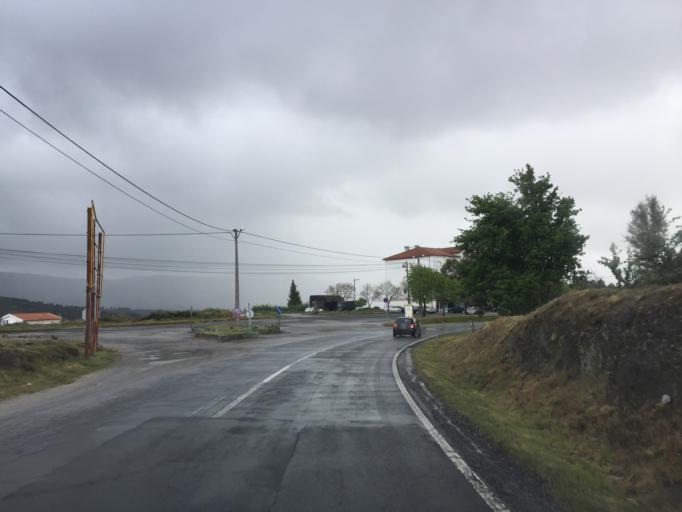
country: PT
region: Guarda
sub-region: Seia
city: Seia
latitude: 40.3873
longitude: -7.7521
